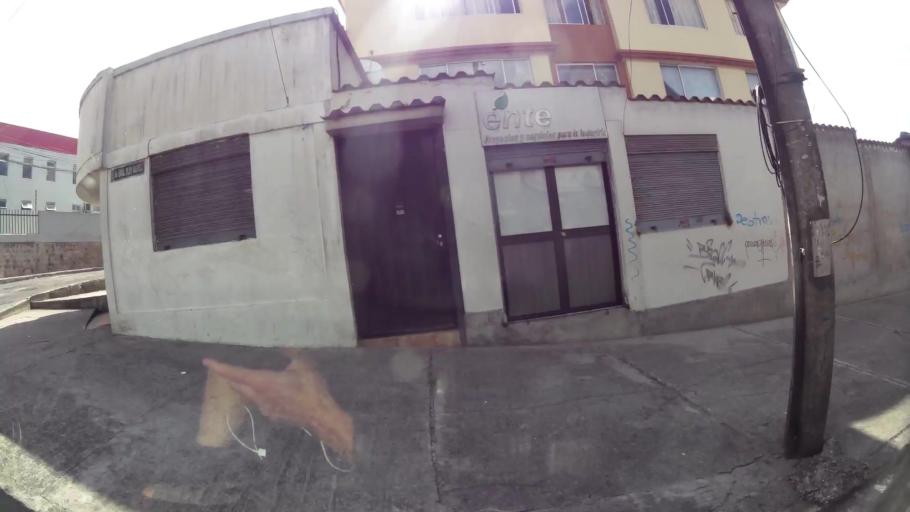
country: EC
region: Pichincha
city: Quito
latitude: -0.1072
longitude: -78.4732
